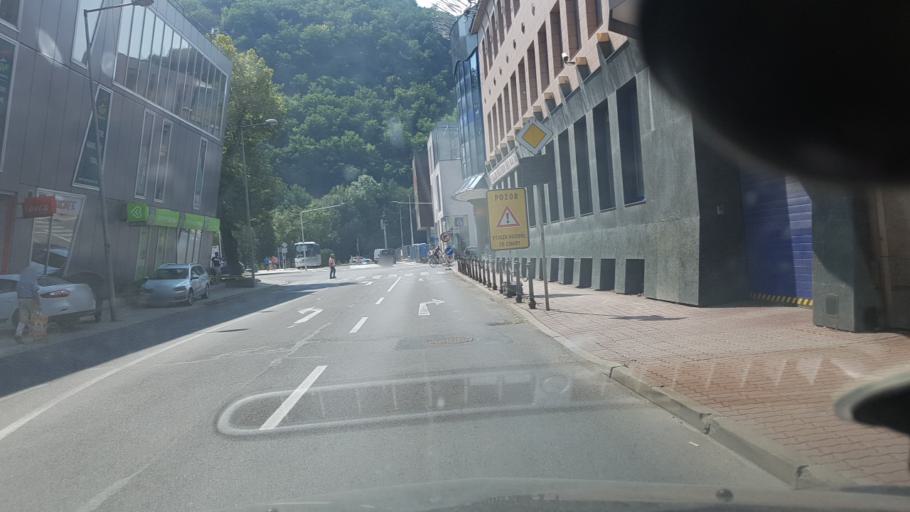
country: SK
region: Banskobystricky
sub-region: Okres Banska Bystrica
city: Banska Bystrica
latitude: 48.7326
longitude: 19.1395
